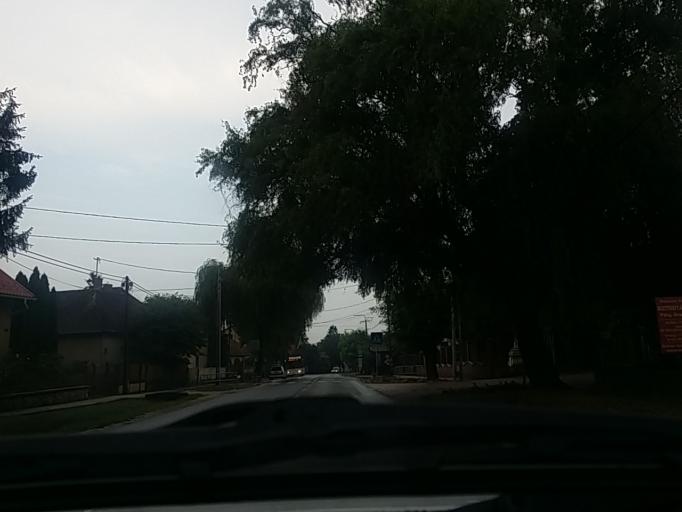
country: HU
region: Pest
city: Paty
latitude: 47.5144
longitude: 18.8273
